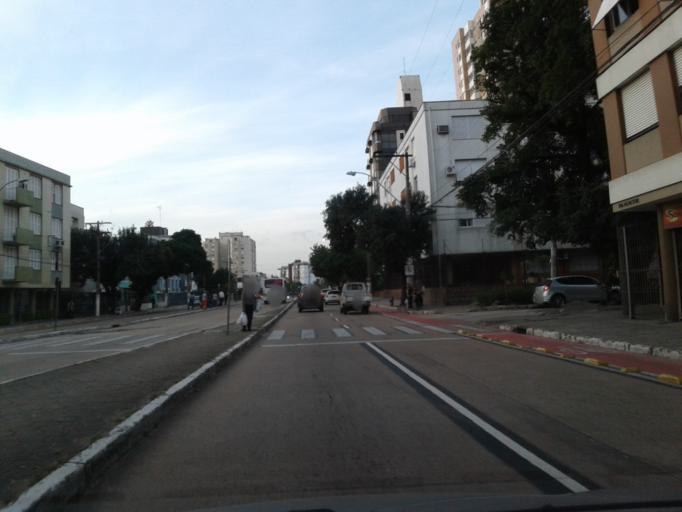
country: BR
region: Rio Grande do Sul
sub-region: Porto Alegre
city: Porto Alegre
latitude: -30.0530
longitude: -51.2183
